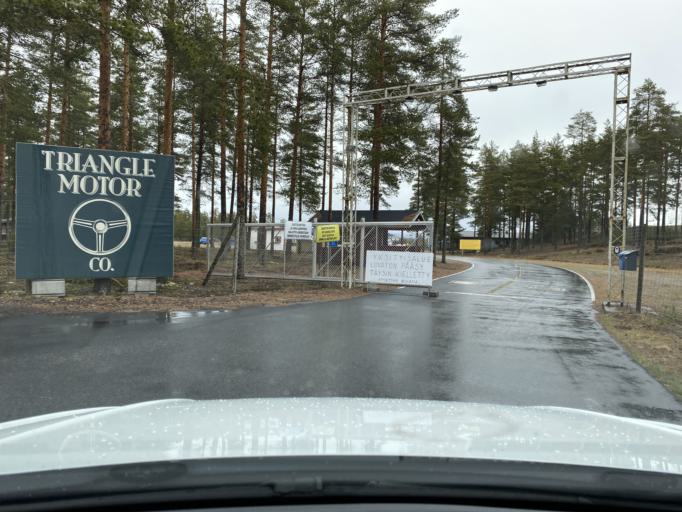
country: FI
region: Satakunta
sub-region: Pori
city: Vampula
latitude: 60.9734
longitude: 22.6553
